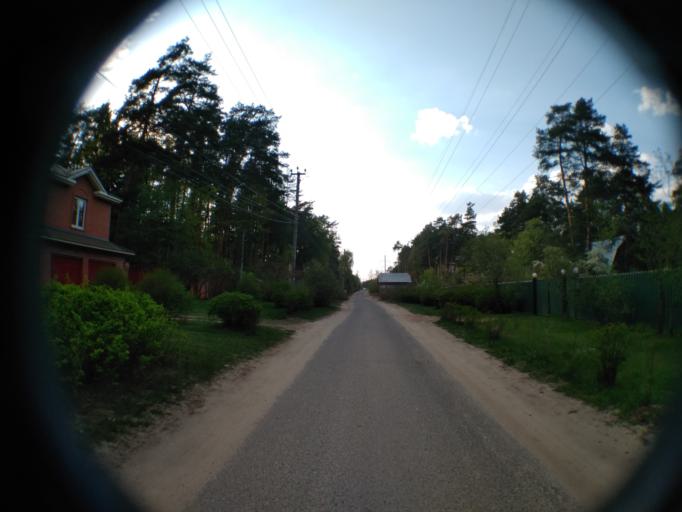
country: RU
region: Moskovskaya
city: Kratovo
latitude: 55.5807
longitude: 38.1640
